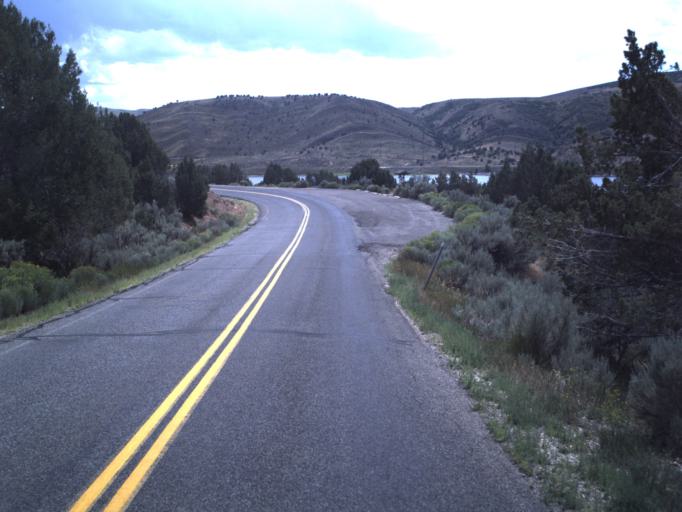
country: US
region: Utah
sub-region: Summit County
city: Oakley
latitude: 40.7695
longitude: -111.3882
